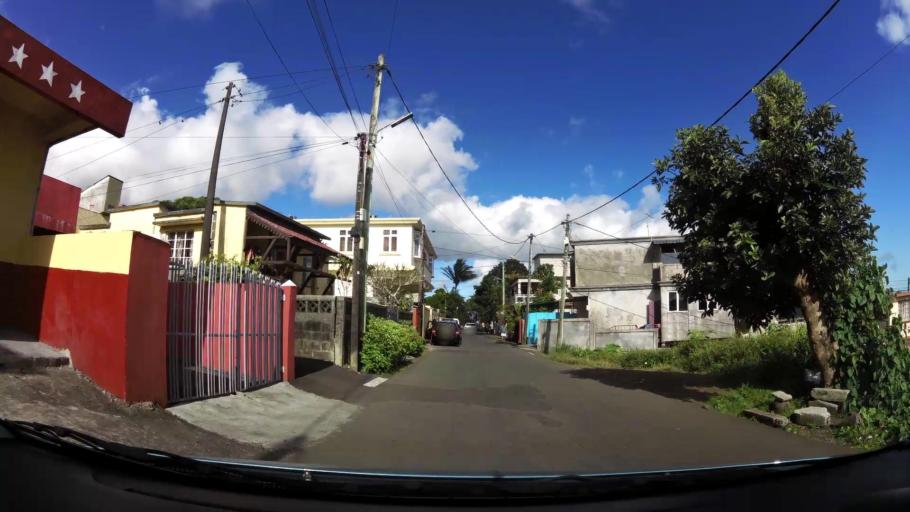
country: MU
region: Plaines Wilhems
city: Curepipe
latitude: -20.3064
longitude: 57.5193
